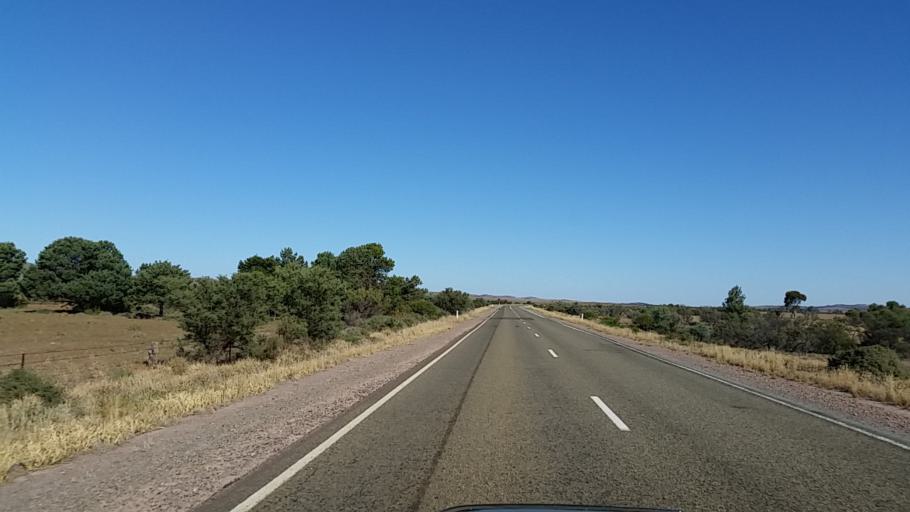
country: AU
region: South Australia
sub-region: Flinders Ranges
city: Quorn
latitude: -32.4348
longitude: 138.5337
